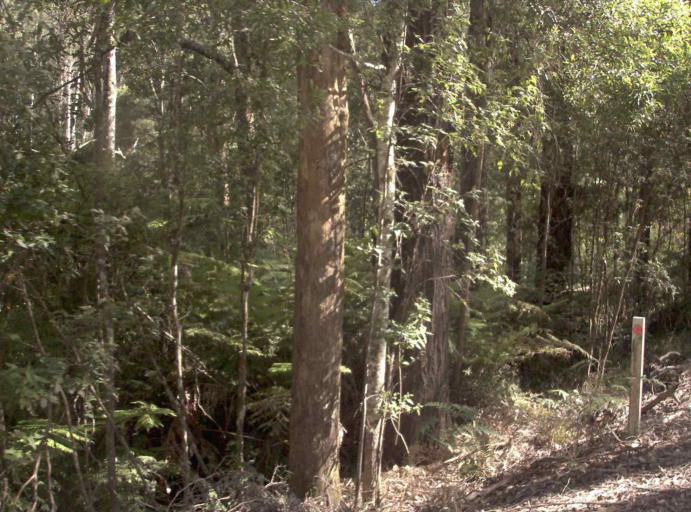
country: AU
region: Victoria
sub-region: East Gippsland
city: Lakes Entrance
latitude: -37.3878
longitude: 148.5991
